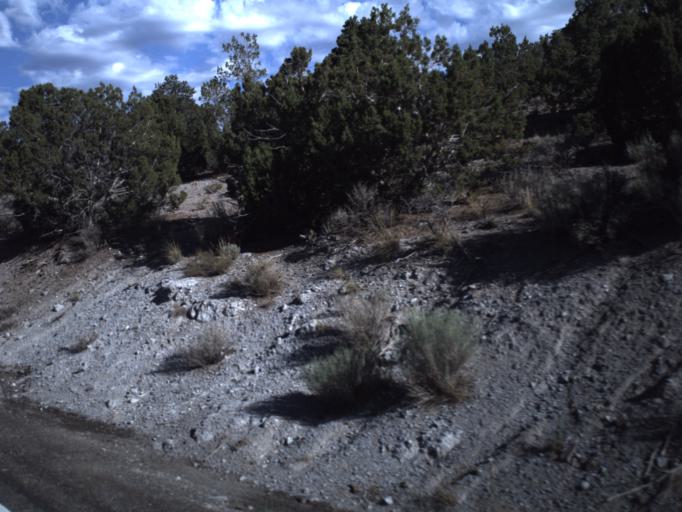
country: US
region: Utah
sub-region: Utah County
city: Genola
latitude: 39.9699
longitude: -112.0598
